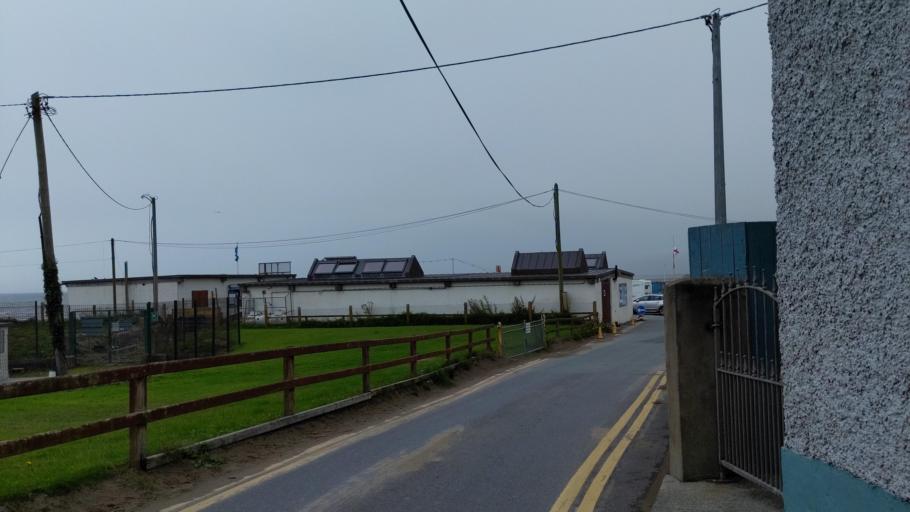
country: IE
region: Leinster
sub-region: Lu
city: Clogherhead
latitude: 53.7893
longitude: -6.2345
